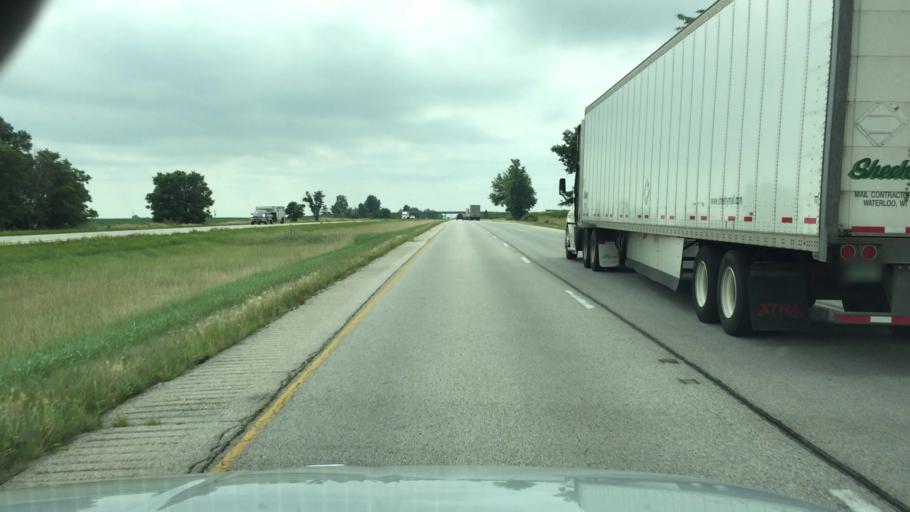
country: US
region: Illinois
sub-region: Knox County
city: Galesburg
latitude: 41.0310
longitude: -90.3347
